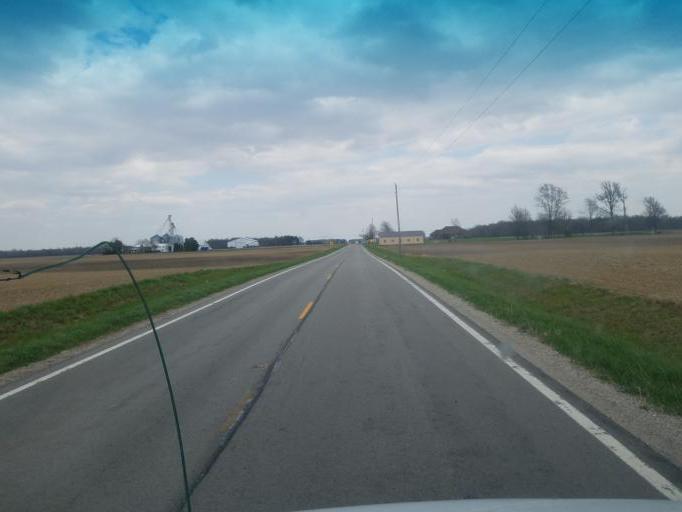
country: US
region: Ohio
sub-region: Crawford County
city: Bucyrus
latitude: 40.9503
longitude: -83.0209
